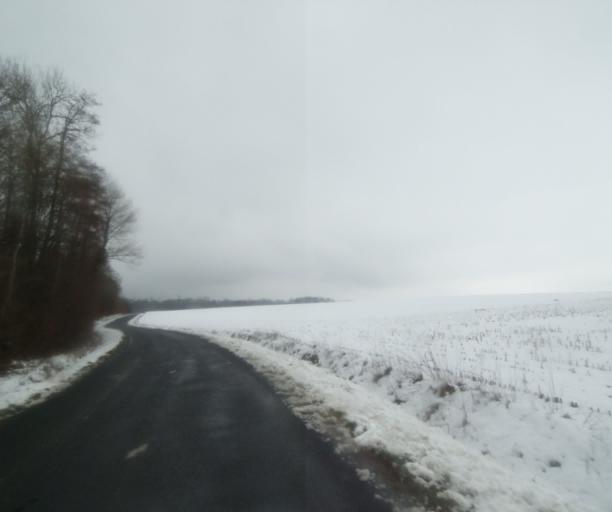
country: FR
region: Champagne-Ardenne
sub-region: Departement de la Haute-Marne
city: Montier-en-Der
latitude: 48.4653
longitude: 4.8182
